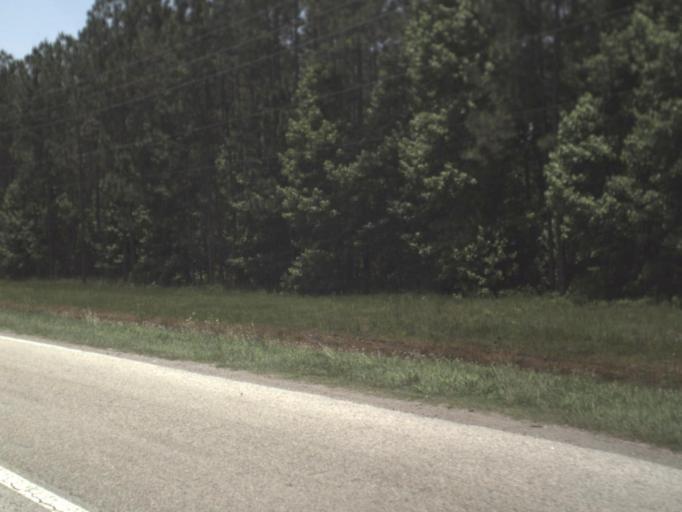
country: US
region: Florida
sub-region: Duval County
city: Baldwin
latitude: 30.2170
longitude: -82.0089
